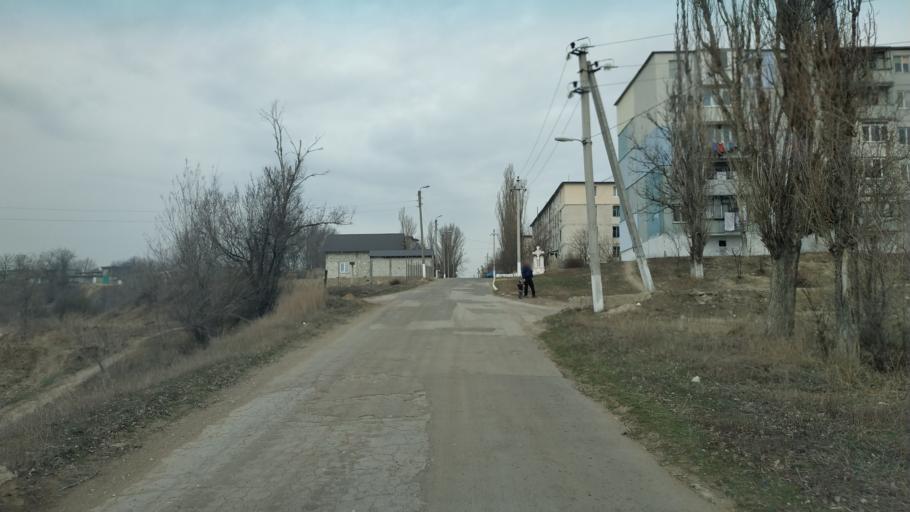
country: MD
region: Chisinau
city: Singera
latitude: 46.9339
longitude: 28.9784
